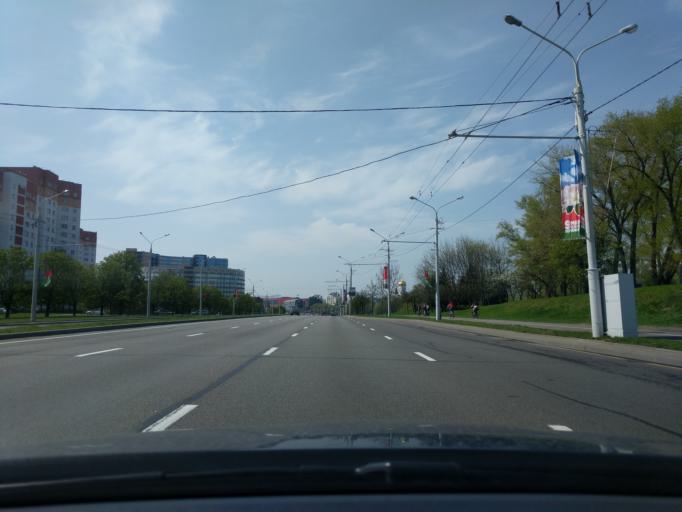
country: BY
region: Minsk
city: Novoye Medvezhino
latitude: 53.9345
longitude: 27.5016
